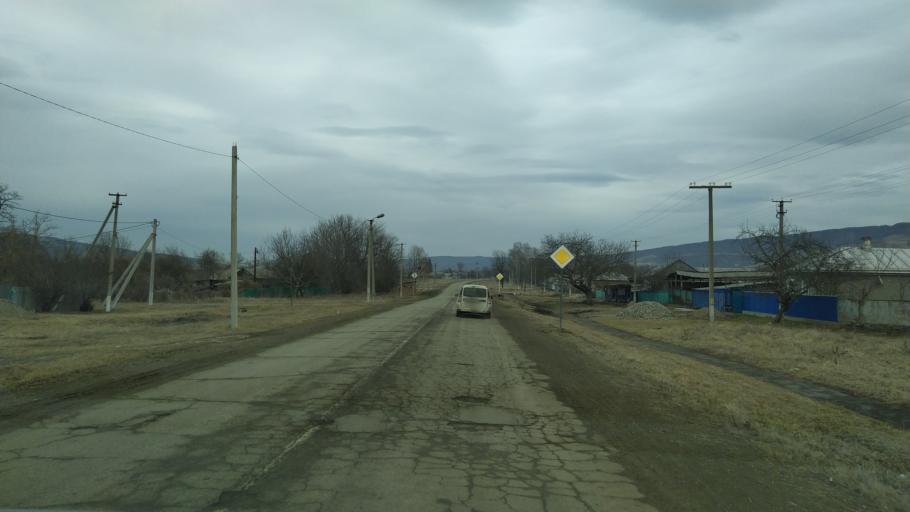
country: RU
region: Krasnodarskiy
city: Peredovaya
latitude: 44.1153
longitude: 41.4592
